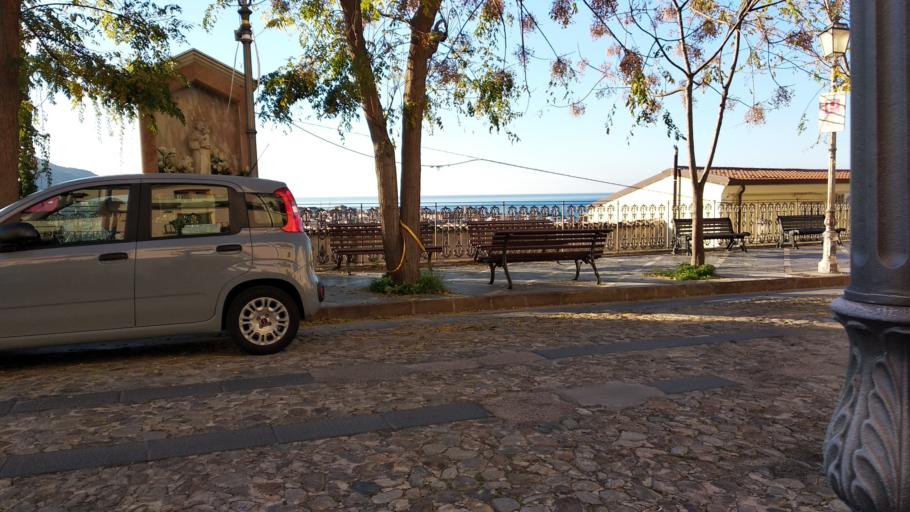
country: IT
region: Calabria
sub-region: Provincia di Cosenza
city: Amantea
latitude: 39.1362
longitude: 16.0764
